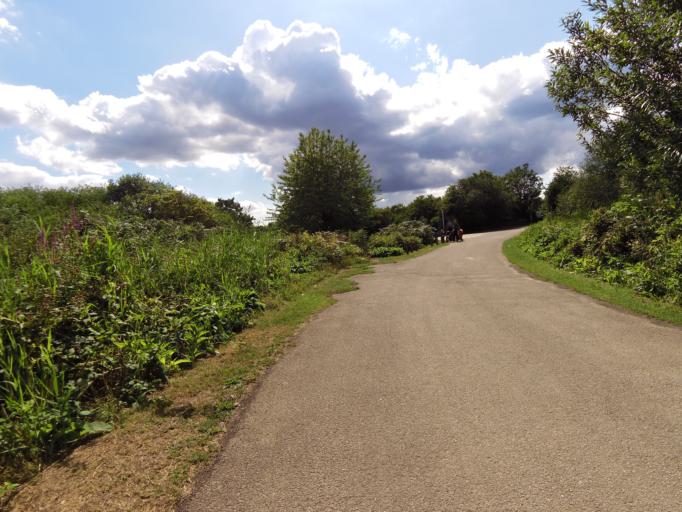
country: GB
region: England
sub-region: Greater London
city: Hackney
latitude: 51.5732
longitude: -0.0551
